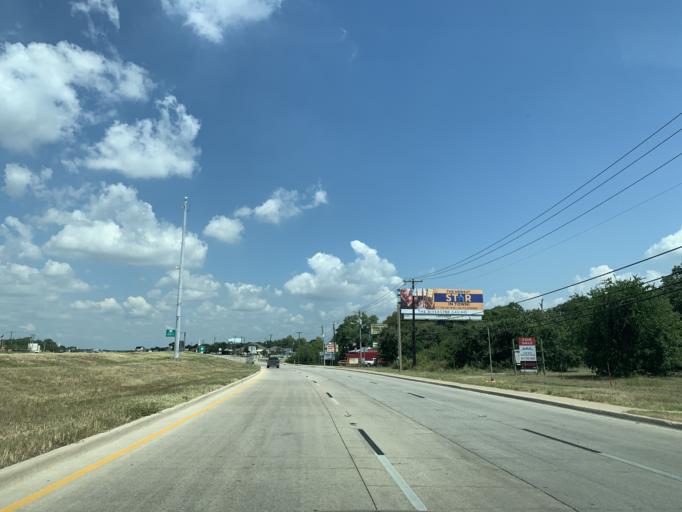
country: US
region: Texas
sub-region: Tarrant County
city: Azle
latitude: 32.8681
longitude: -97.5236
